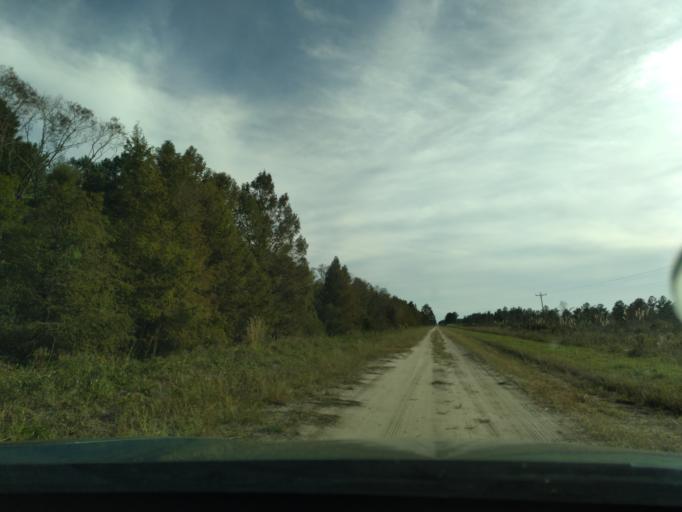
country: US
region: North Carolina
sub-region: Beaufort County
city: Belhaven
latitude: 35.6892
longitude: -76.5433
